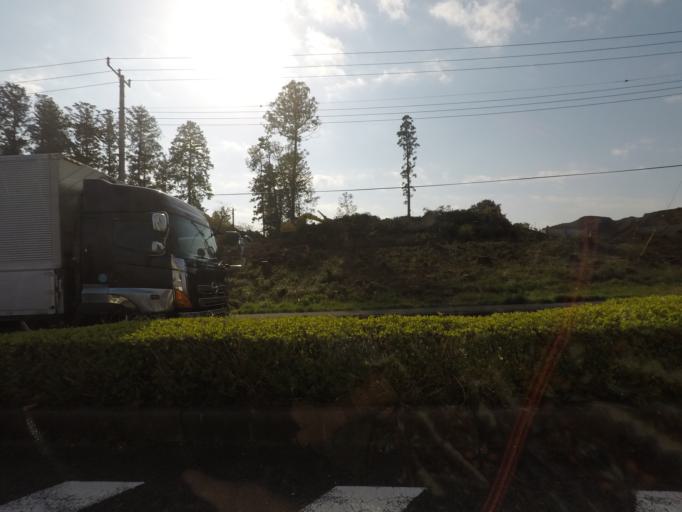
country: JP
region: Chiba
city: Narita
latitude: 35.7689
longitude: 140.3115
